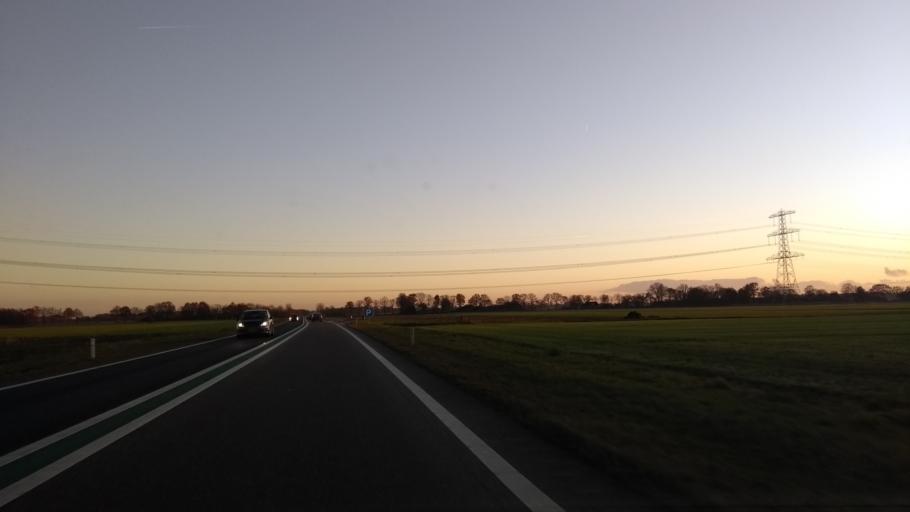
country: NL
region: Overijssel
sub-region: Gemeente Twenterand
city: Den Ham
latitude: 52.5816
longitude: 6.4136
